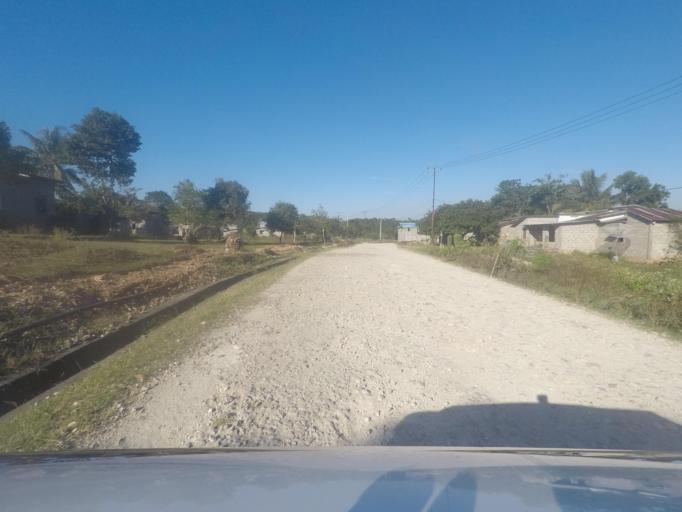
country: TL
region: Lautem
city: Lospalos
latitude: -8.3995
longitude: 127.1965
